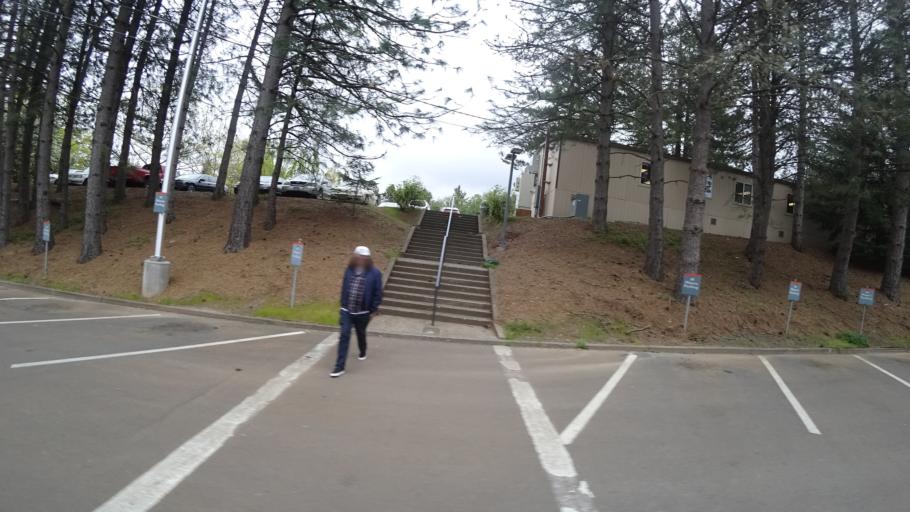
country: US
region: Oregon
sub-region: Washington County
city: Metzger
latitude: 45.4399
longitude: -122.7310
